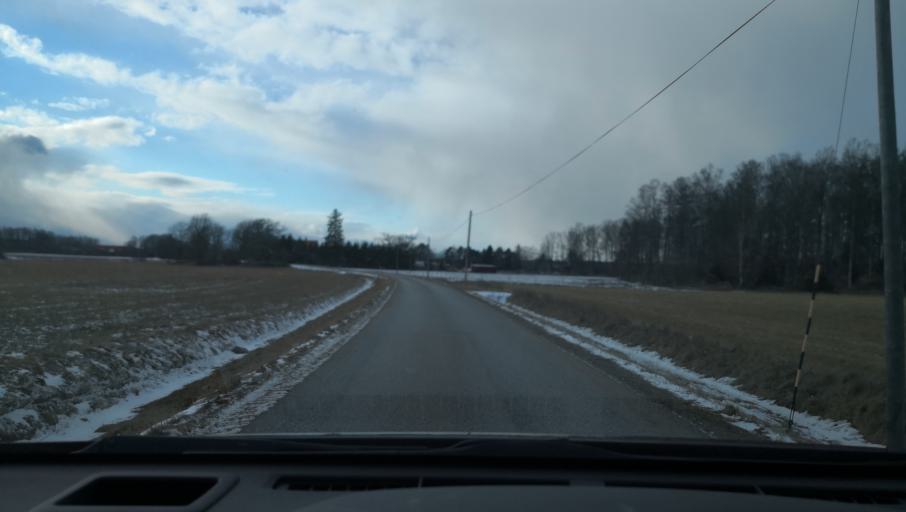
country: SE
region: Uppsala
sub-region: Enkopings Kommun
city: Irsta
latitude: 59.7021
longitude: 16.9375
